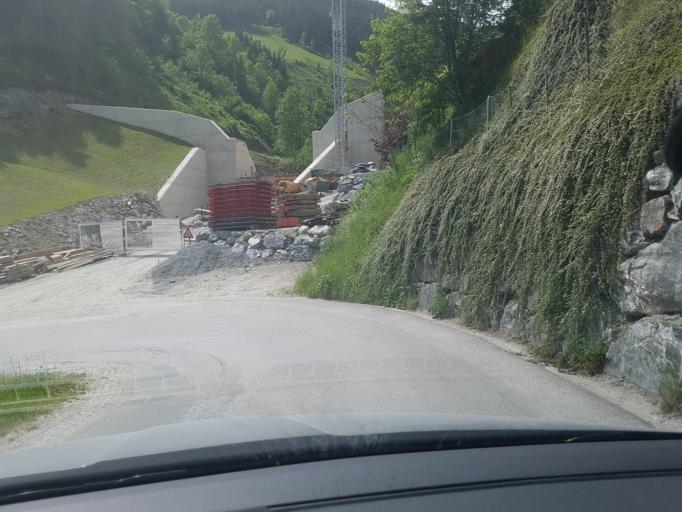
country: AT
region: Salzburg
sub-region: Politischer Bezirk Sankt Johann im Pongau
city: Schwarzach im Pongau
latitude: 47.2675
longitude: 13.2007
